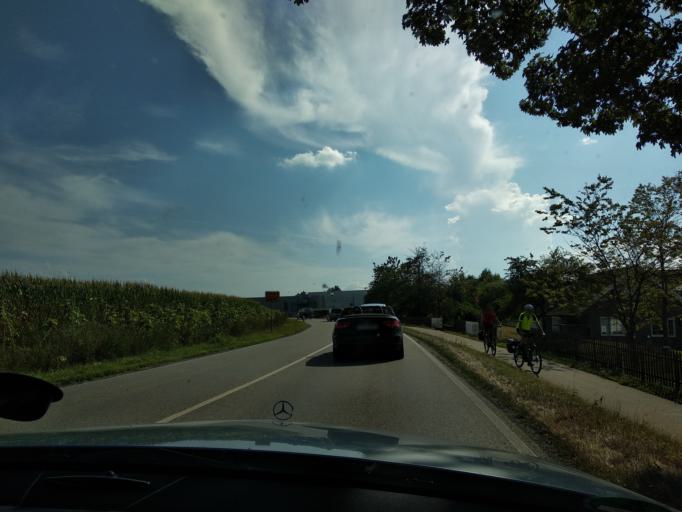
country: DE
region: Baden-Wuerttemberg
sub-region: Tuebingen Region
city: Amtzell
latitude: 47.6933
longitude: 9.7589
